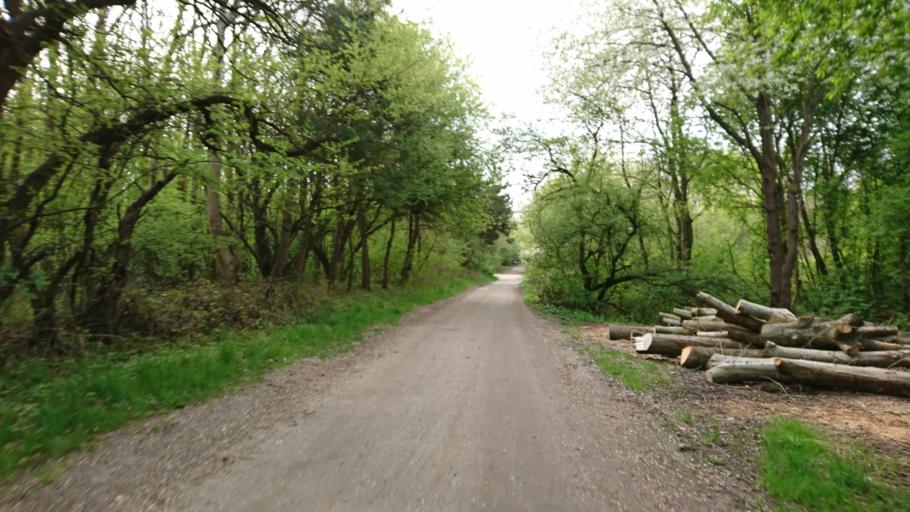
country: DK
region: Capital Region
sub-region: Ballerup Kommune
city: Ballerup
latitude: 55.7450
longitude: 12.3987
